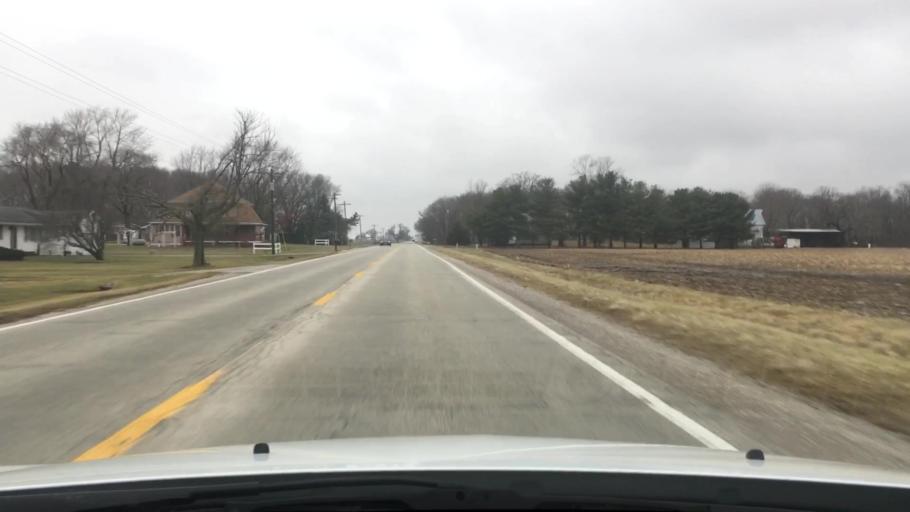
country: US
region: Illinois
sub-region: Iroquois County
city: Clifton
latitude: 40.8879
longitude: -87.8285
